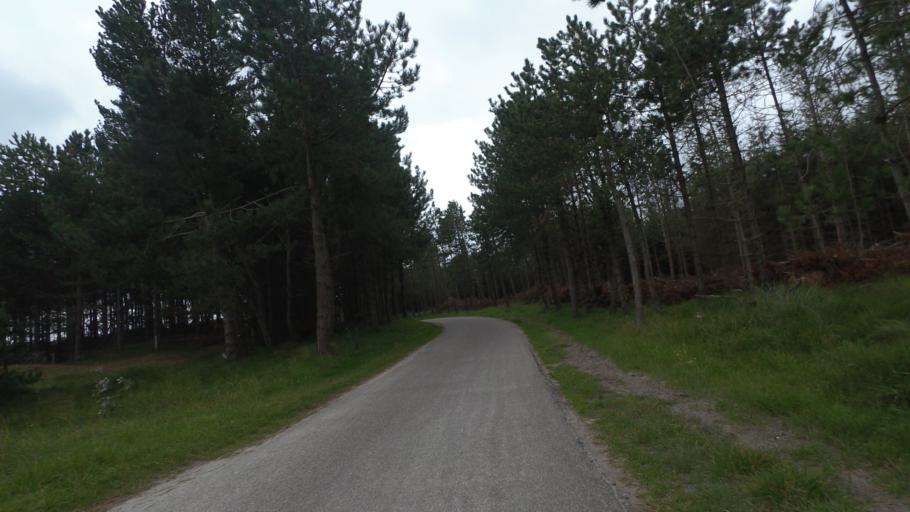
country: NL
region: Friesland
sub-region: Gemeente Ameland
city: Nes
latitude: 53.4505
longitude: 5.7842
